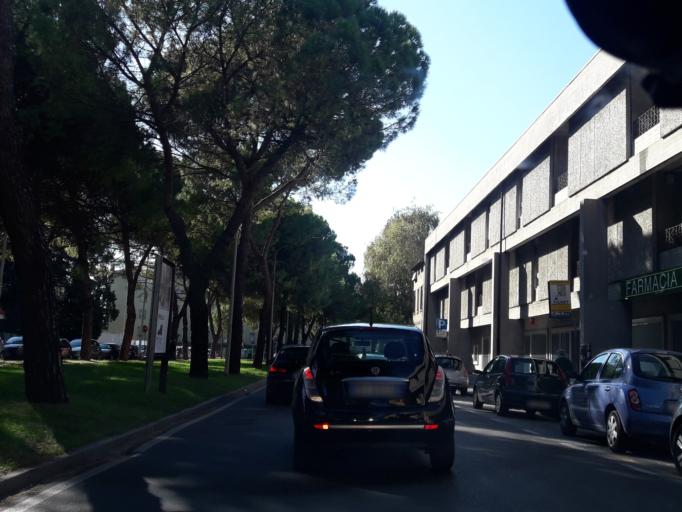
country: IT
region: Friuli Venezia Giulia
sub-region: Provincia di Udine
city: Udine
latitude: 46.0562
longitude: 13.2344
